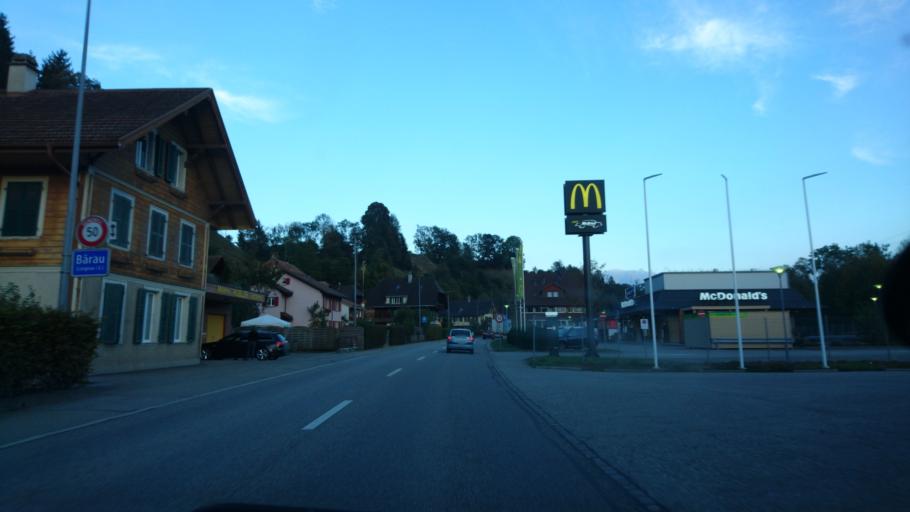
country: CH
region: Bern
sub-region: Emmental District
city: Langnau
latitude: 46.9384
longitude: 7.7999
